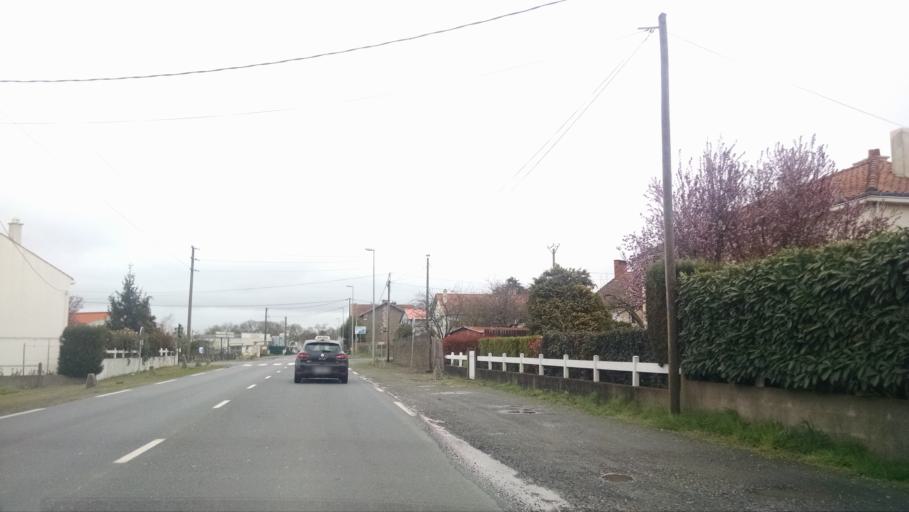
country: FR
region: Pays de la Loire
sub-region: Departement de la Loire-Atlantique
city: Vallet
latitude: 47.1611
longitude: -1.2766
